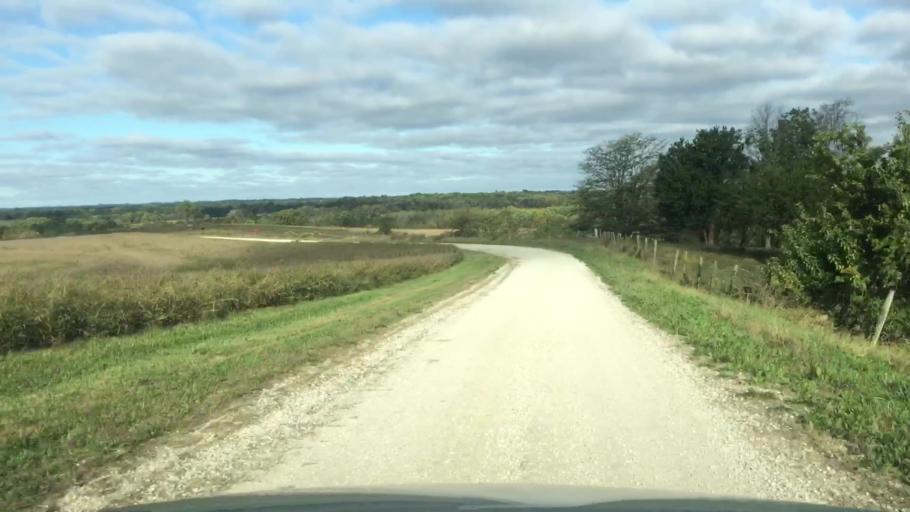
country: US
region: Missouri
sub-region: Howard County
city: New Franklin
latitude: 39.0826
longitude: -92.7520
